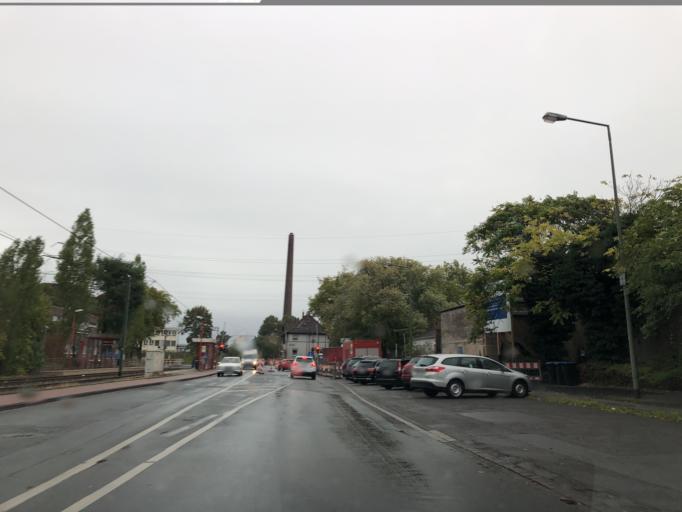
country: DE
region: North Rhine-Westphalia
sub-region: Regierungsbezirk Dusseldorf
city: Hochfeld
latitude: 51.3724
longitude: 6.7329
